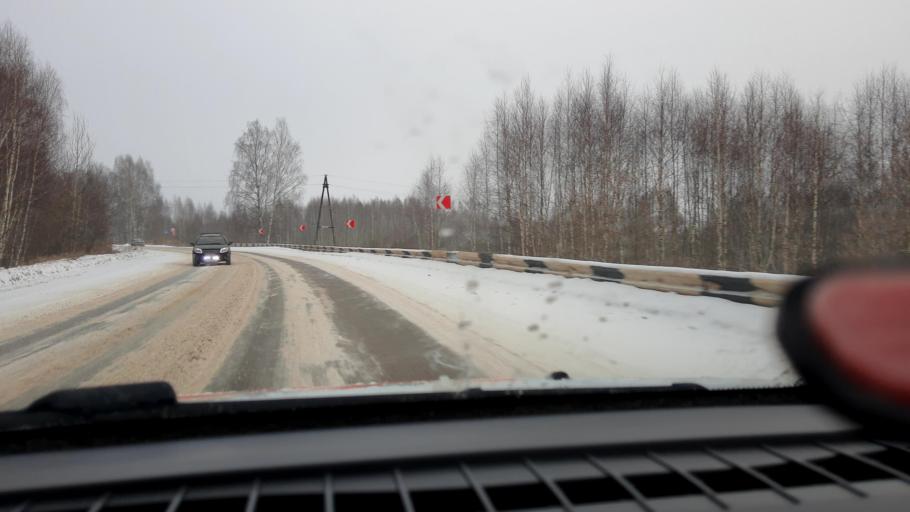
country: RU
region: Nizjnij Novgorod
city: Afonino
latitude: 56.3127
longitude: 44.2219
